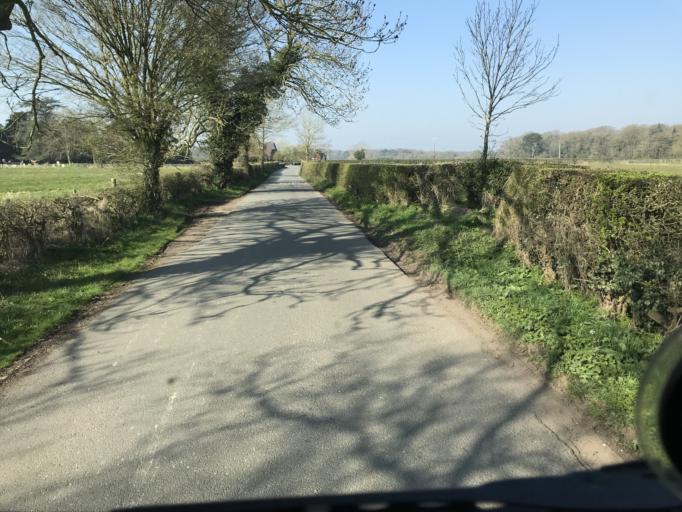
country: GB
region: England
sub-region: Cheshire West and Chester
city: Aldford
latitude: 53.1401
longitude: -2.8395
